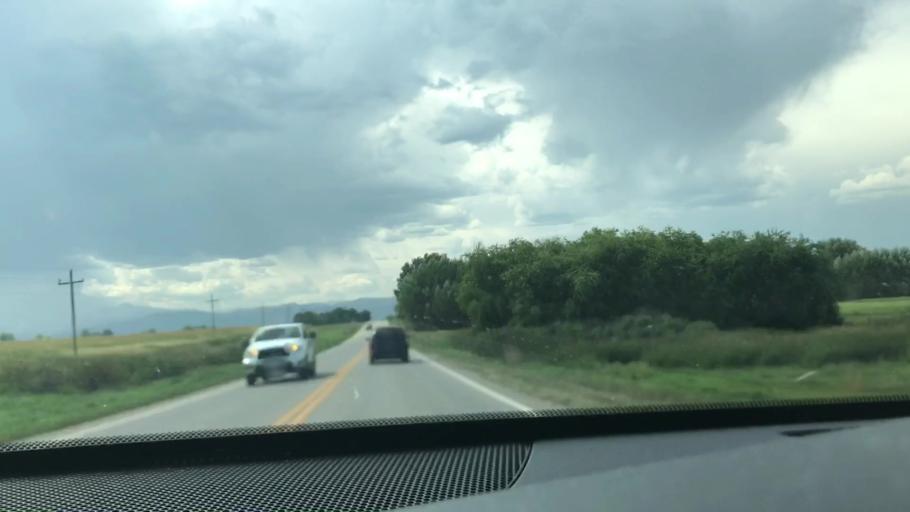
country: US
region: Colorado
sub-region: Larimer County
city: Loveland
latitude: 40.3795
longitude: -105.0046
